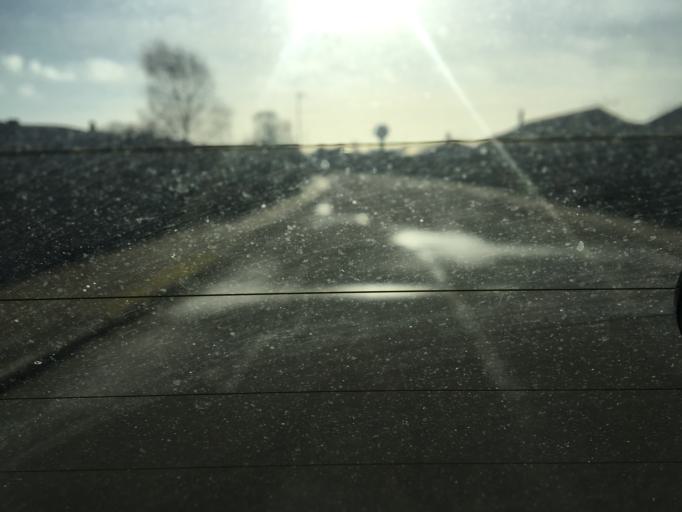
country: DK
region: Capital Region
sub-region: Tarnby Kommune
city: Tarnby
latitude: 55.6163
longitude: 12.6260
